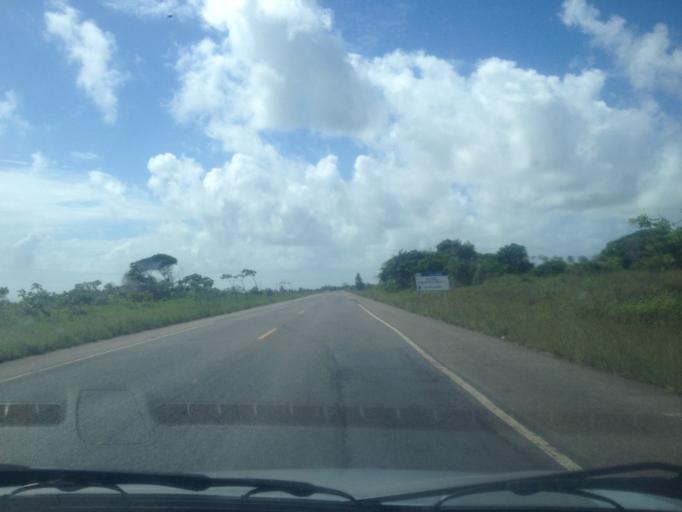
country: BR
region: Bahia
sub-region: Conde
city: Conde
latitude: -11.8739
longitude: -37.6384
